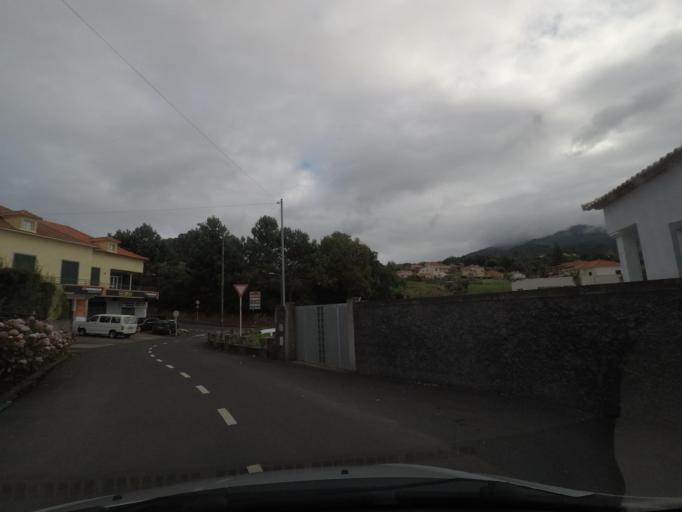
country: PT
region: Madeira
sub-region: Santana
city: Santana
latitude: 32.8055
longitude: -16.8780
